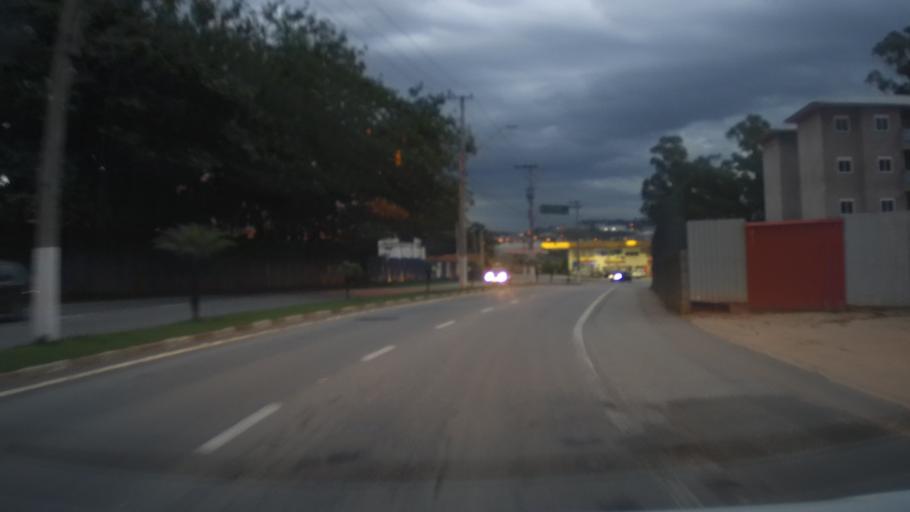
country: BR
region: Sao Paulo
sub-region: Vinhedo
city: Vinhedo
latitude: -23.0389
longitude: -46.9999
